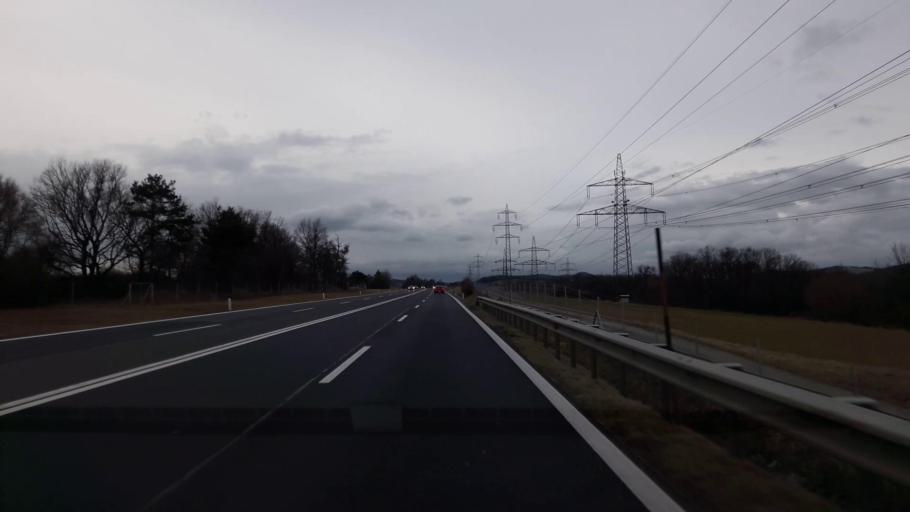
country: AT
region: Burgenland
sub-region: Politischer Bezirk Oberpullendorf
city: Kobersdorf
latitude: 47.6046
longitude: 16.3989
